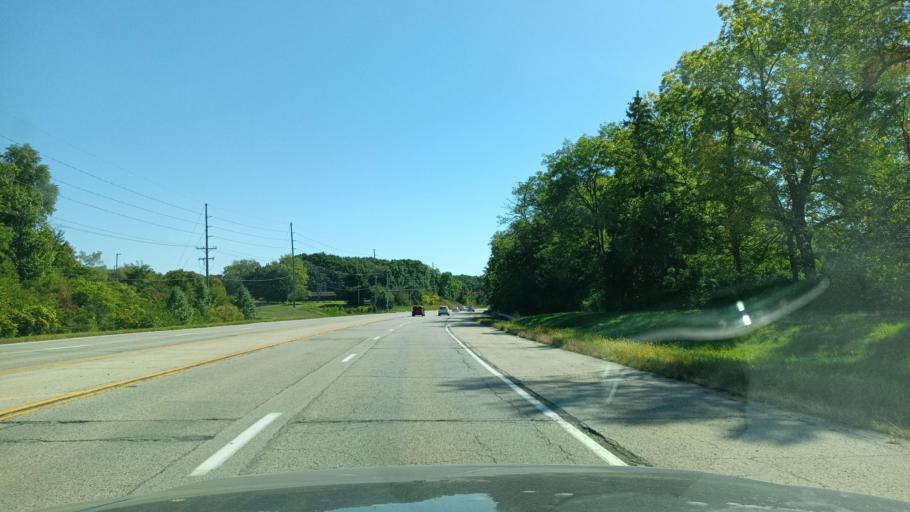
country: US
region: Illinois
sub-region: Peoria County
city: Peoria Heights
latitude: 40.7686
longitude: -89.6480
